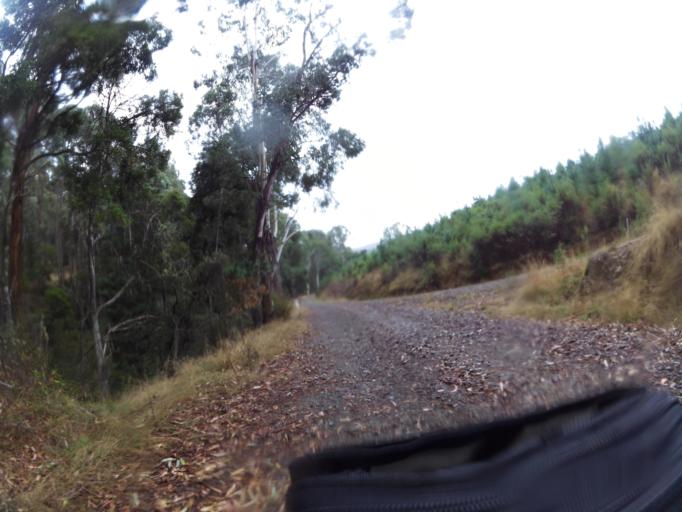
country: AU
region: New South Wales
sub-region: Greater Hume Shire
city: Holbrook
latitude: -36.2158
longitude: 147.5660
